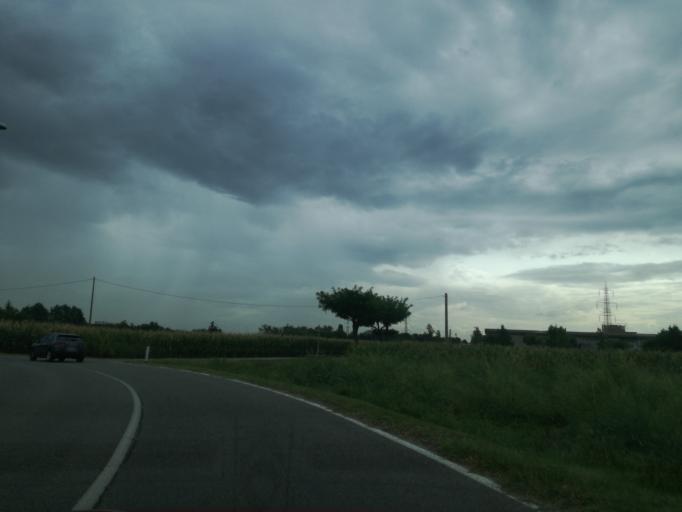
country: IT
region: Lombardy
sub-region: Provincia di Monza e Brianza
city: Mezzago
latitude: 45.6220
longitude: 9.4383
